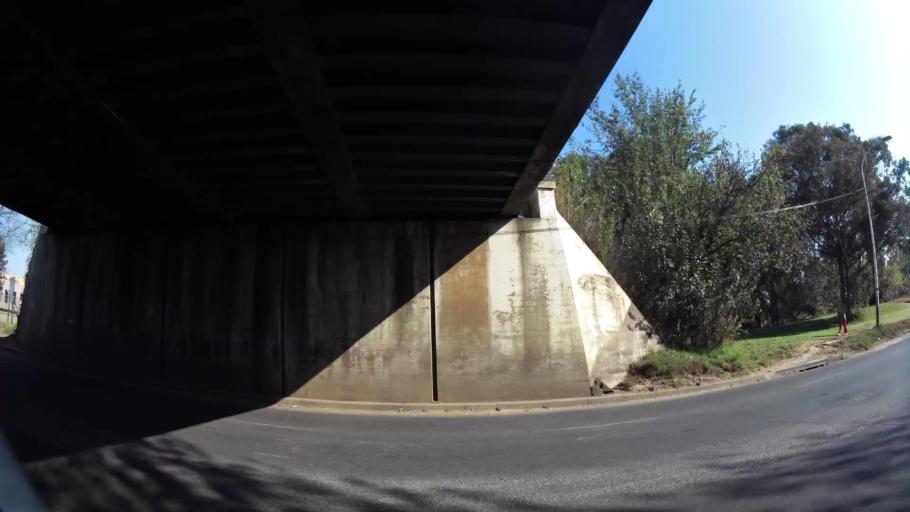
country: ZA
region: Gauteng
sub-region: Ekurhuleni Metropolitan Municipality
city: Boksburg
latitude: -26.2189
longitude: 28.2533
